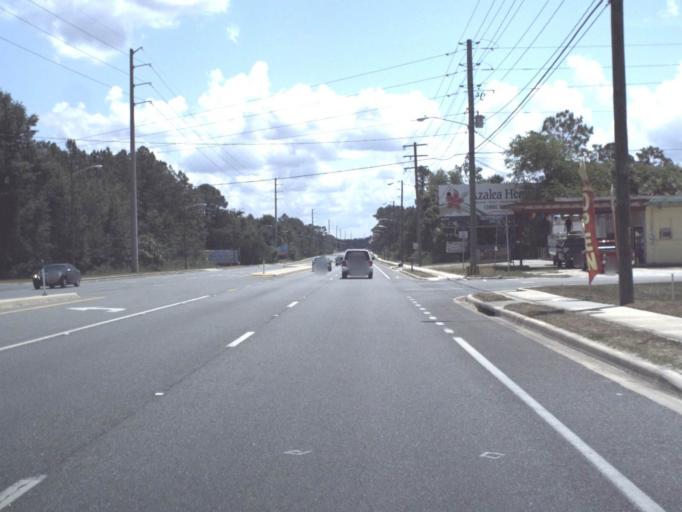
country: US
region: Florida
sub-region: Putnam County
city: Palatka
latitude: 29.6361
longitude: -81.7043
